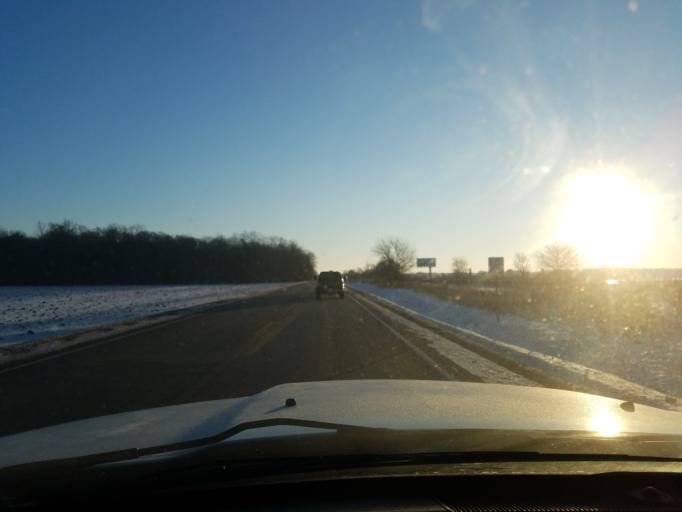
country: US
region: Indiana
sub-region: Elkhart County
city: Nappanee
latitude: 41.4456
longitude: -86.0618
